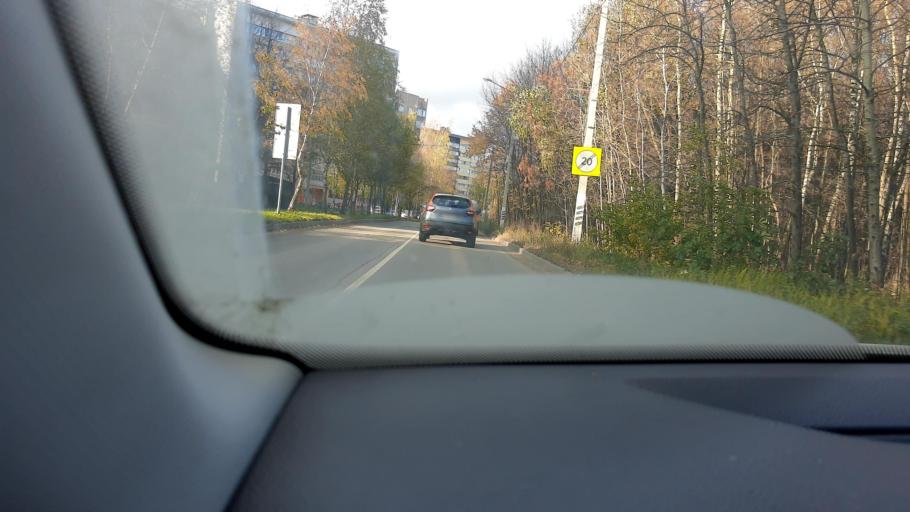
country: RU
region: Moskovskaya
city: Shcherbinka
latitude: 55.5339
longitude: 37.5873
